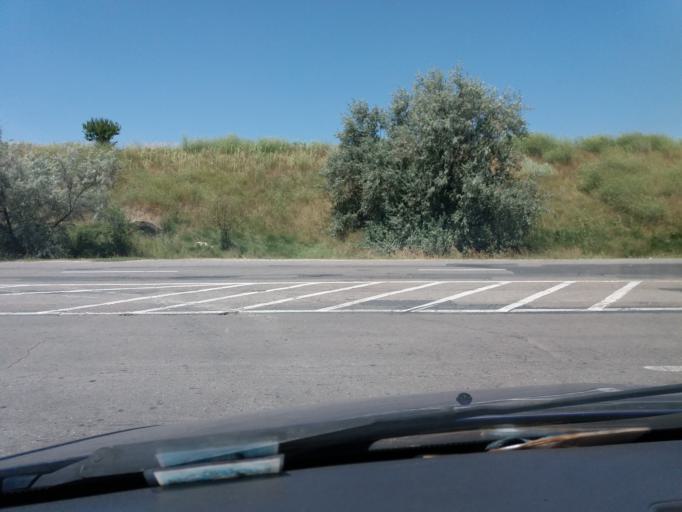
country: RO
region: Constanta
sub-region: Comuna Navodari
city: Navodari
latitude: 44.3286
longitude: 28.6277
